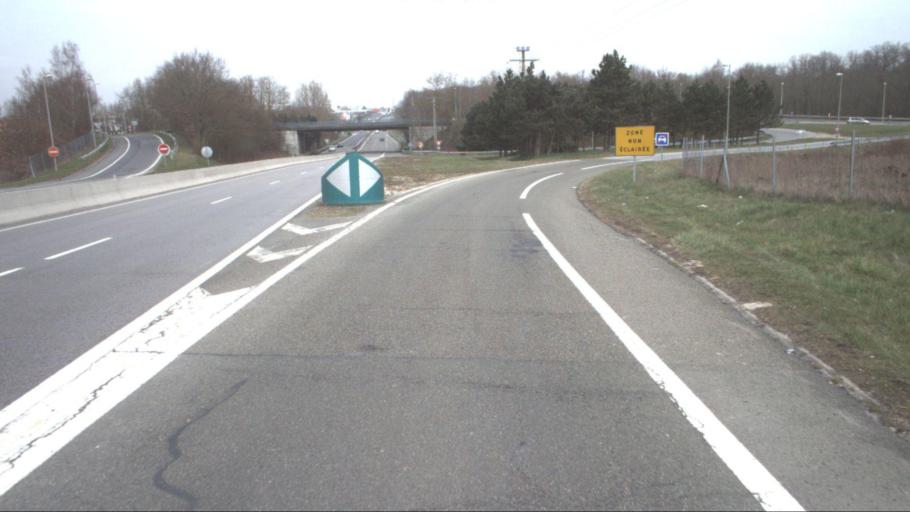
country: FR
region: Ile-de-France
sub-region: Departement des Yvelines
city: Rambouillet
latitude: 48.6187
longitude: 1.8313
